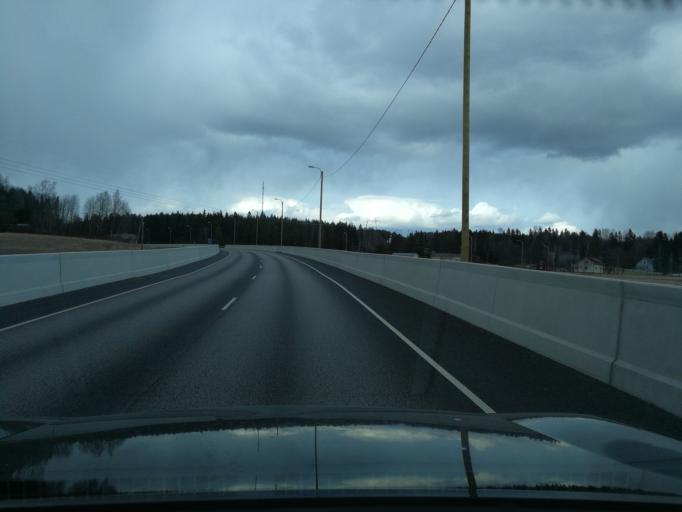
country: FI
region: Varsinais-Suomi
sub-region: Salo
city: Salo
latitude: 60.3772
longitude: 23.1751
